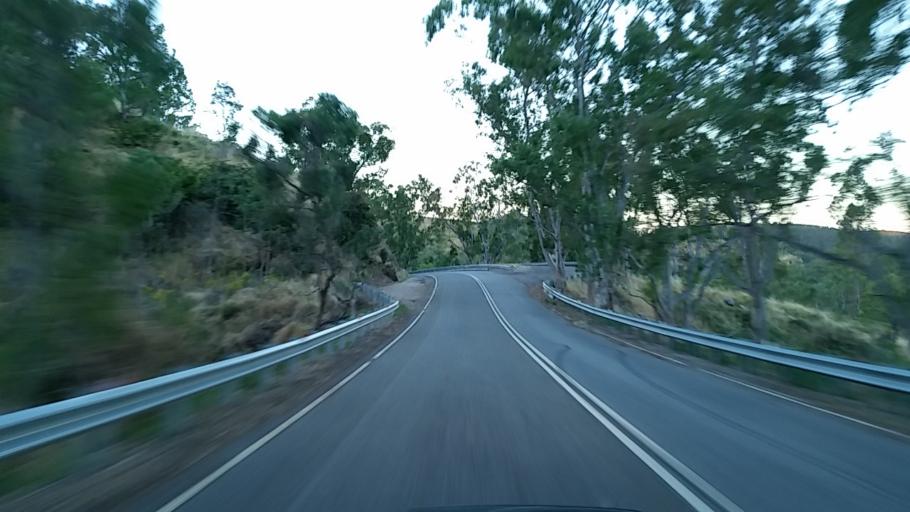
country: AU
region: South Australia
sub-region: Campbelltown
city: Athelstone
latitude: -34.8561
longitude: 138.7907
